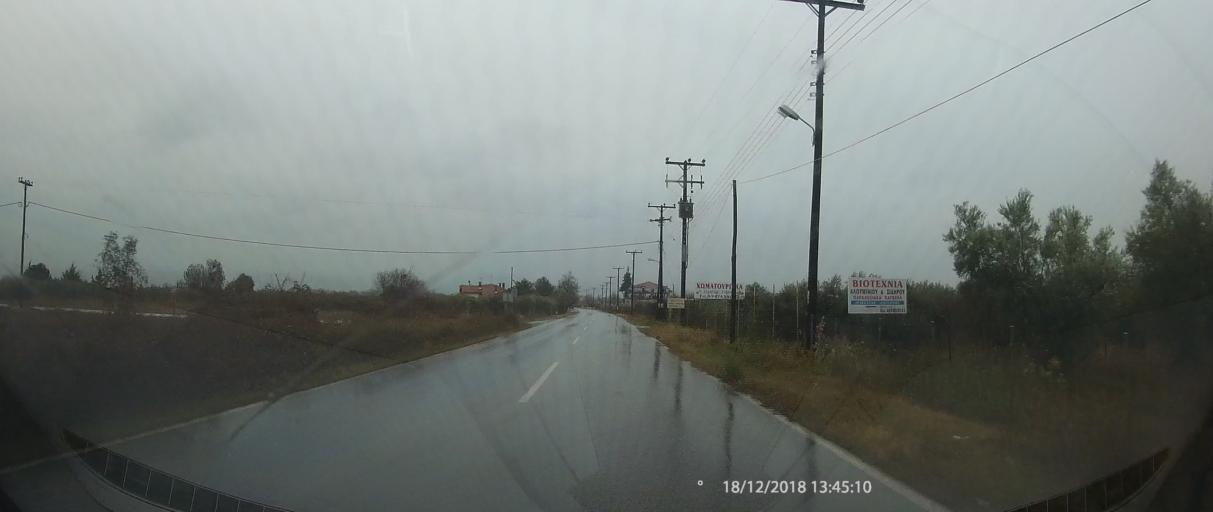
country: GR
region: Central Macedonia
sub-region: Nomos Pierias
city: Litochoro
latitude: 40.0988
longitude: 22.5409
